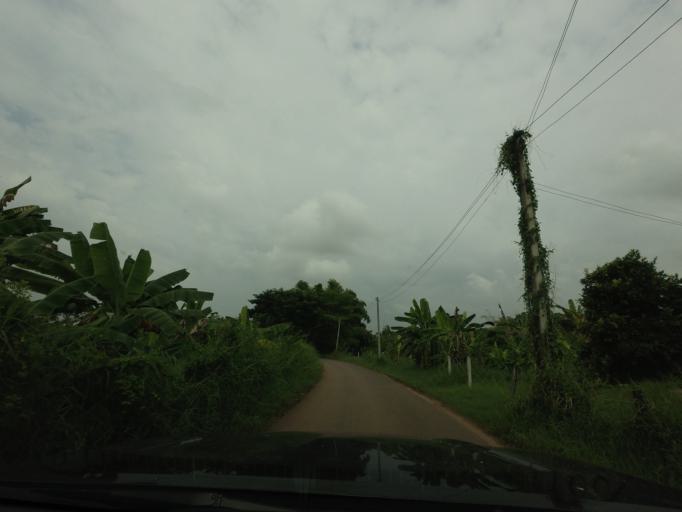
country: TH
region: Nong Khai
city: Nong Khai
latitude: 17.8170
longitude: 102.7078
